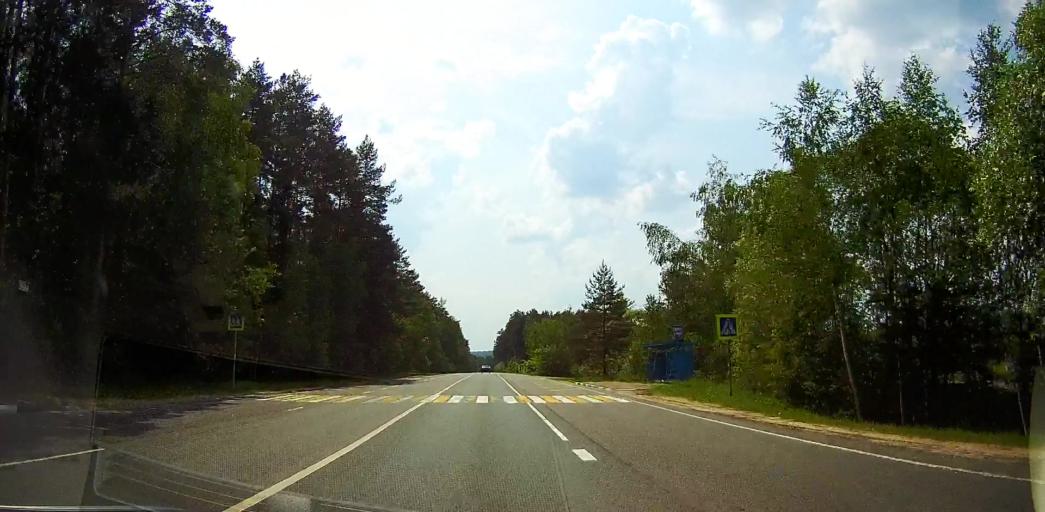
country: RU
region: Moskovskaya
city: Stupino
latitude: 54.9760
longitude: 38.1576
